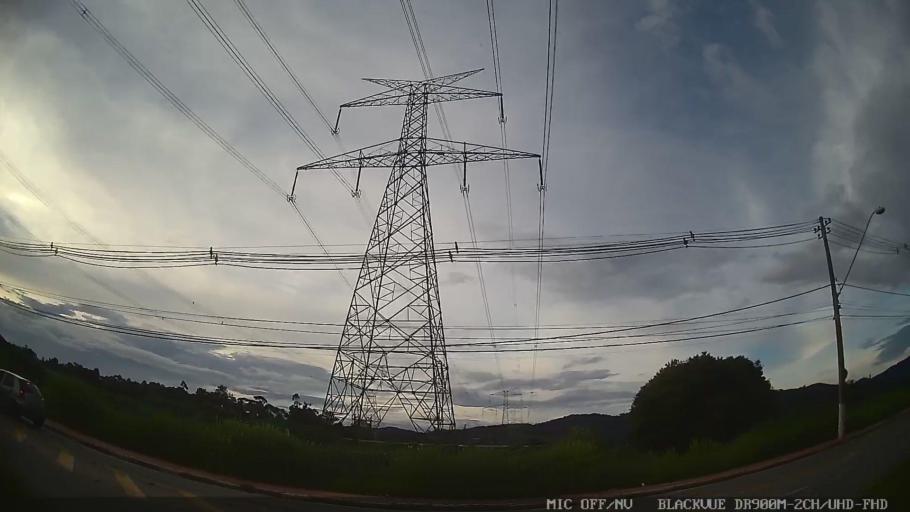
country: BR
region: Sao Paulo
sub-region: Mogi das Cruzes
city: Mogi das Cruzes
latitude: -23.5431
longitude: -46.2447
